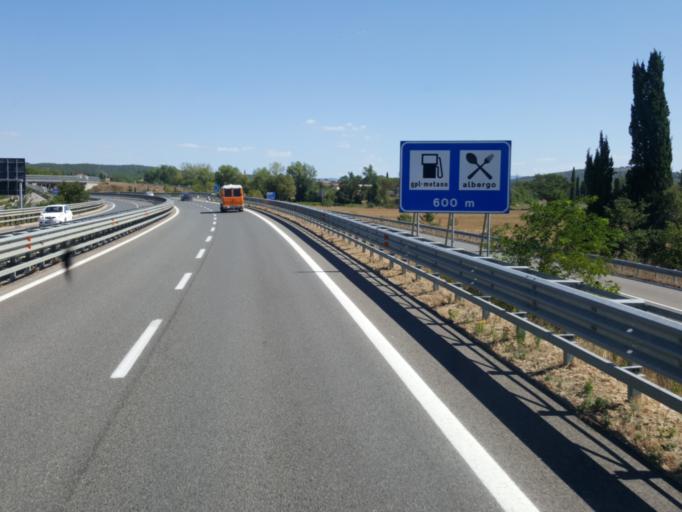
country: IT
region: Tuscany
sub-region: Provincia di Grosseto
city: Campagnatico
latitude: 42.9231
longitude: 11.2632
